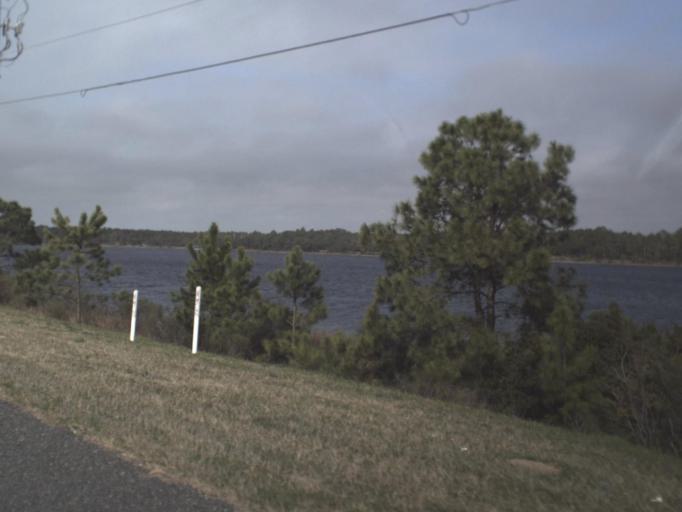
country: US
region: Florida
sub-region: Bay County
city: Laguna Beach
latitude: 30.2716
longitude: -85.9826
